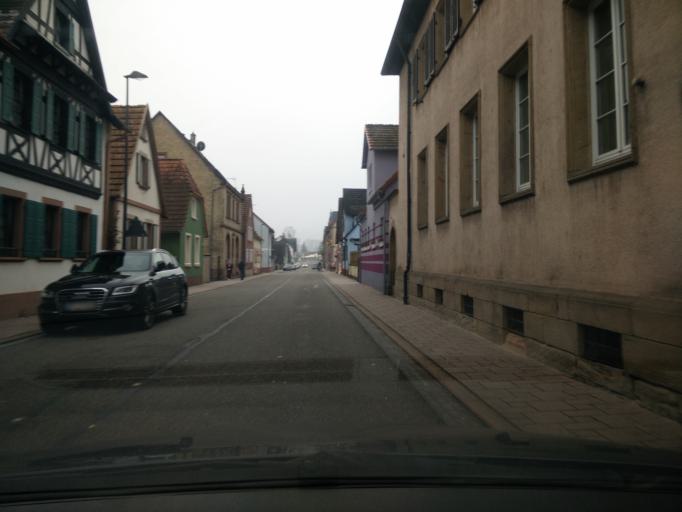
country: DE
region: Rheinland-Pfalz
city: Kandel
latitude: 49.0821
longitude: 8.1992
